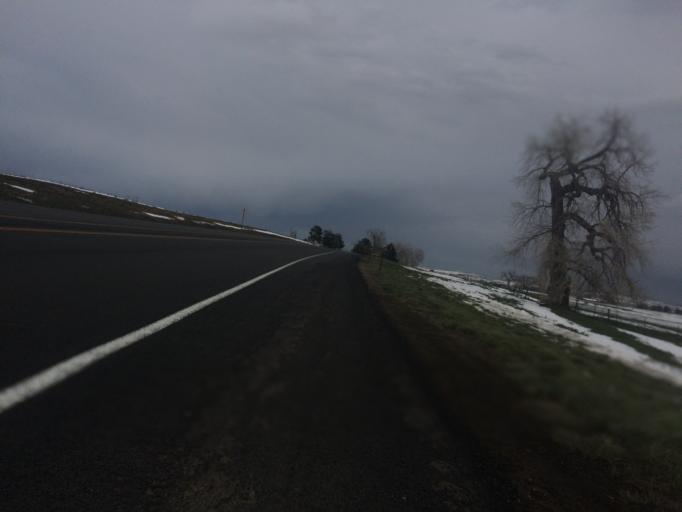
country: US
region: Colorado
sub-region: Boulder County
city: Superior
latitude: 39.9572
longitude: -105.1455
